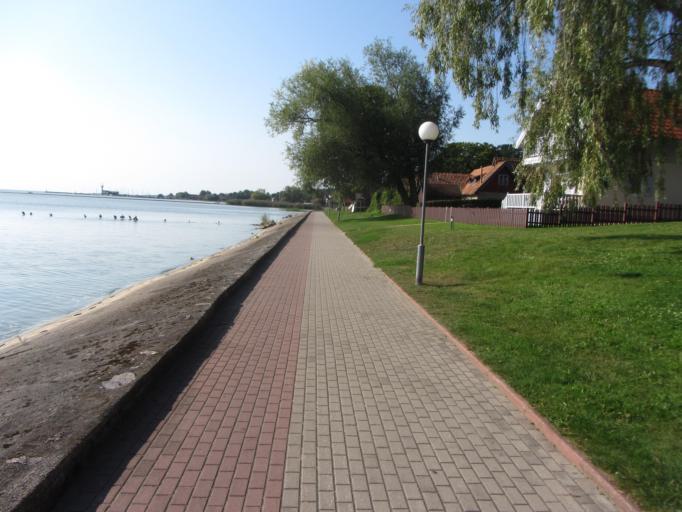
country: LT
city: Nida
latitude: 55.3126
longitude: 21.0133
